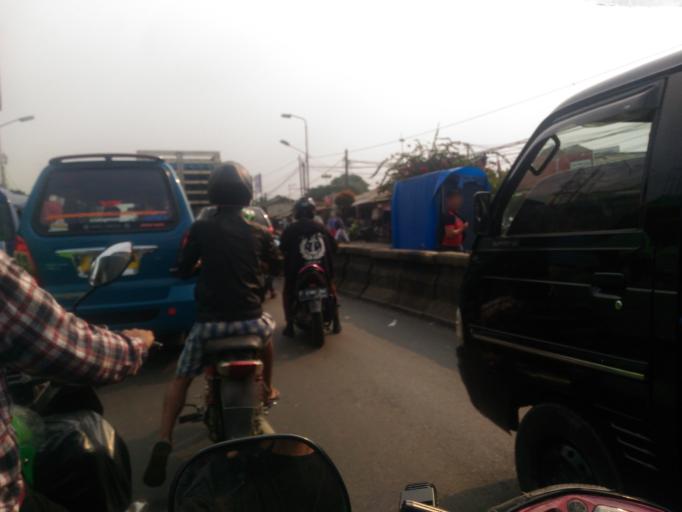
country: ID
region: West Java
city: Caringin
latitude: -6.6560
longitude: 106.8471
